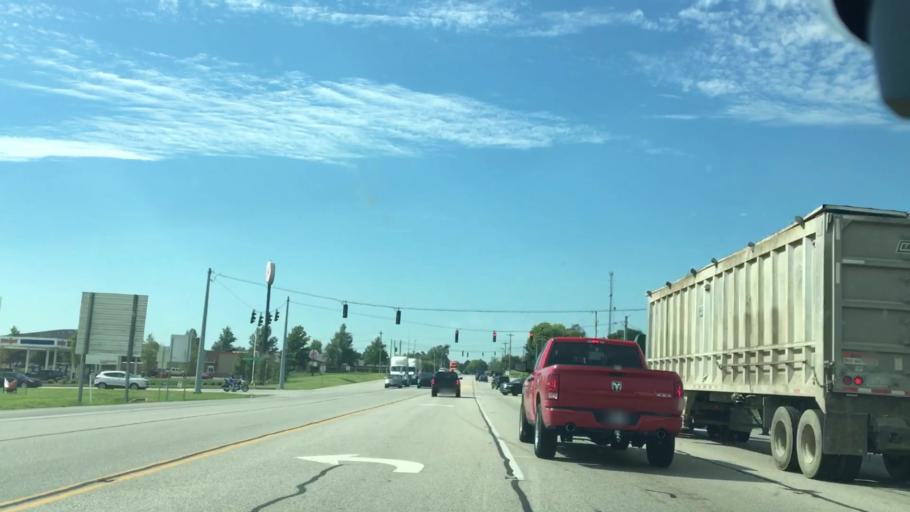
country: US
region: Kentucky
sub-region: Daviess County
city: Owensboro
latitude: 37.7581
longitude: -87.0722
